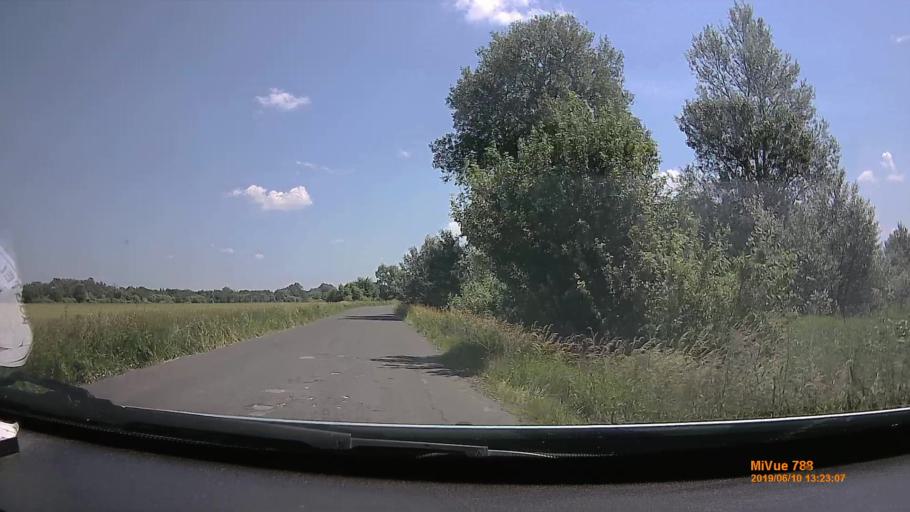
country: HU
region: Borsod-Abauj-Zemplen
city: Tiszaluc
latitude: 48.0272
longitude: 21.0902
